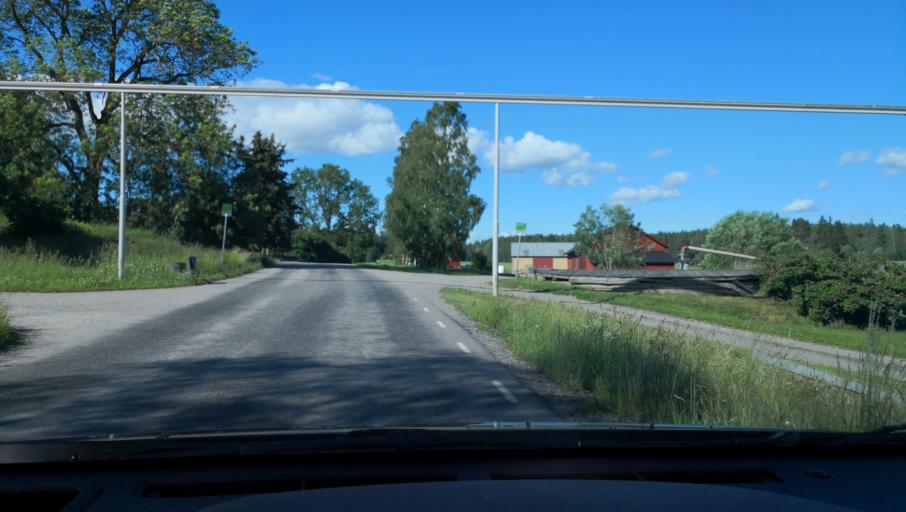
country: SE
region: Soedermanland
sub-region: Eskilstuna Kommun
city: Arla
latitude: 59.3207
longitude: 16.6091
